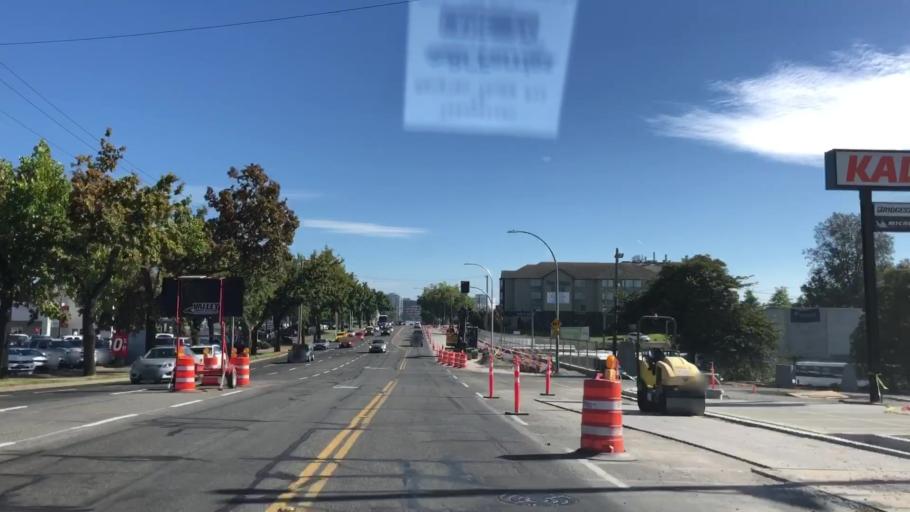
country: CA
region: British Columbia
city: Victoria
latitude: 48.4414
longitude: -123.3687
